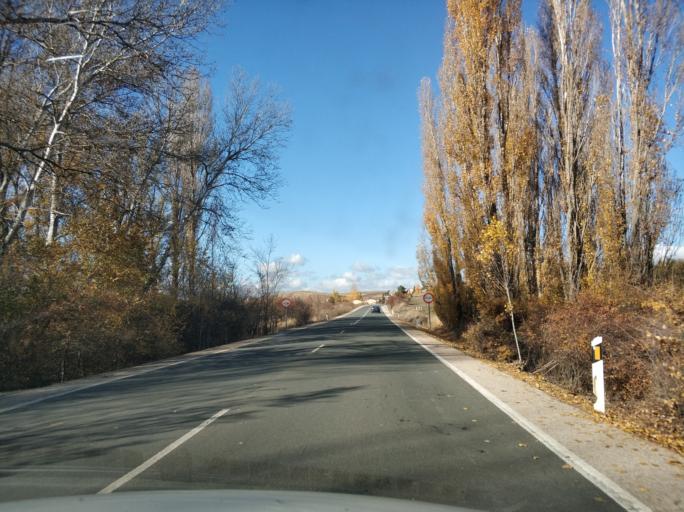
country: ES
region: Castille and Leon
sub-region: Provincia de Soria
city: Almazan
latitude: 41.4729
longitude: -2.5283
